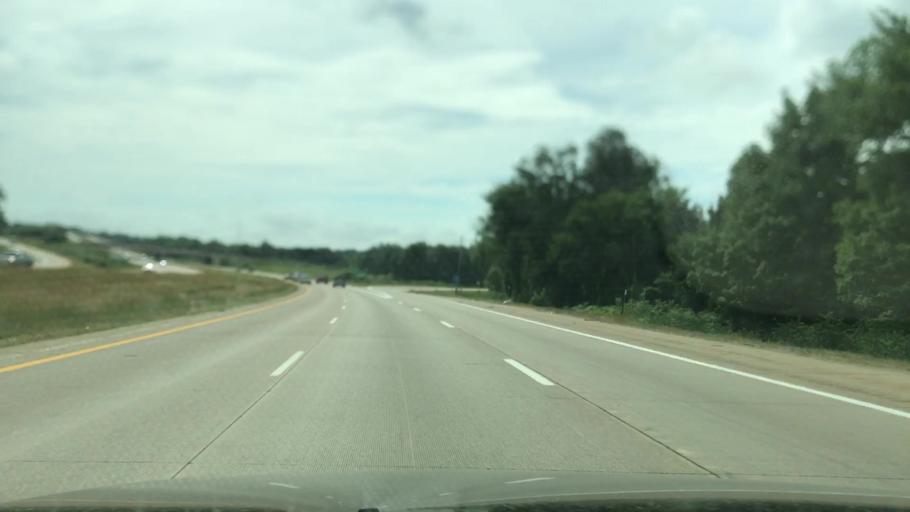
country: US
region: Michigan
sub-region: Kent County
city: Comstock Park
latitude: 43.0219
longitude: -85.7194
